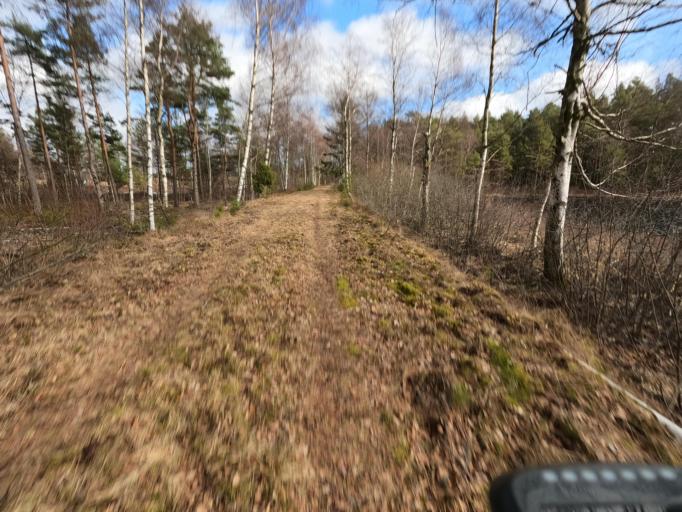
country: SE
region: Kronoberg
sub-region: Alvesta Kommun
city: Vislanda
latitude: 56.8226
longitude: 14.3131
